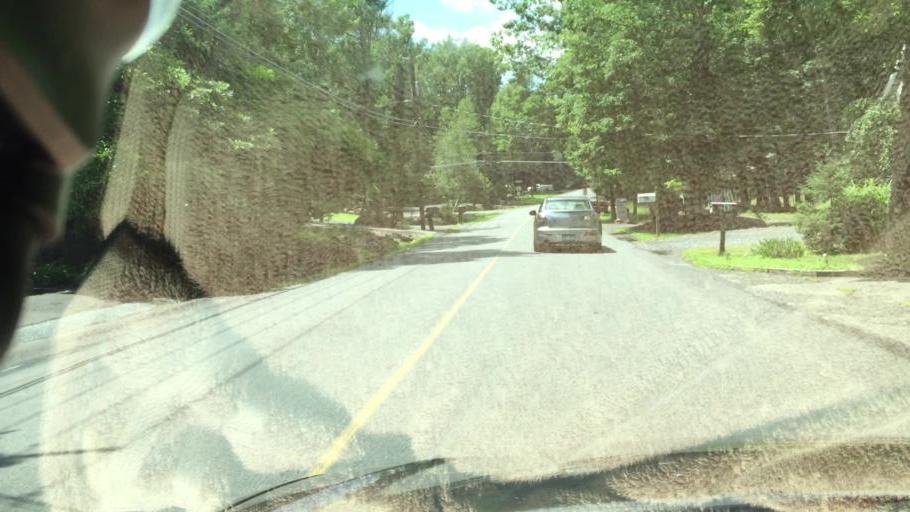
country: US
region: Pennsylvania
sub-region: Luzerne County
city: Freeland
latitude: 41.0448
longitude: -75.9281
